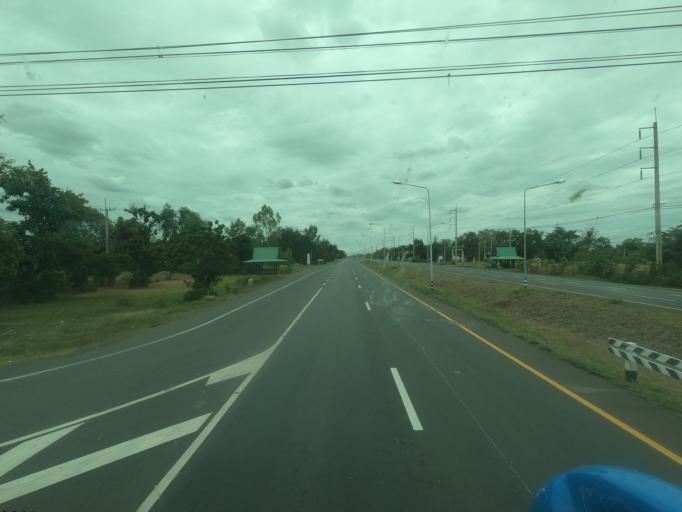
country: TH
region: Buriram
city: Chaloem Phra Kiat
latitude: 14.6069
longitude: 102.9718
